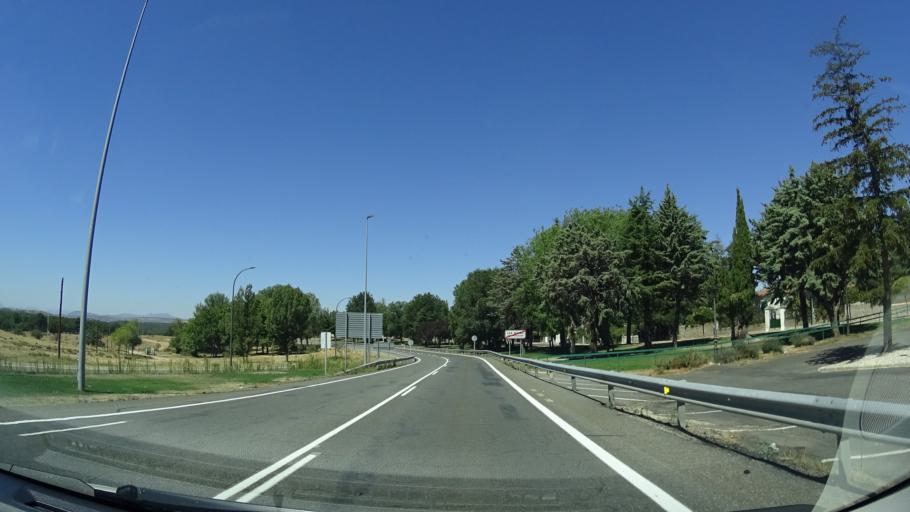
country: ES
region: Castille and Leon
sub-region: Provincia de Avila
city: Las Navas del Marques
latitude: 40.5981
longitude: -4.3397
